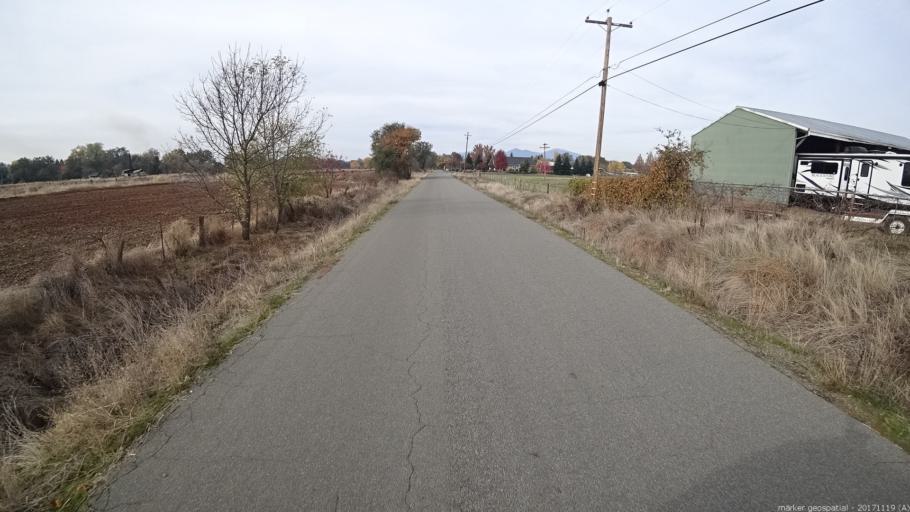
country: US
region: California
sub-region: Shasta County
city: Anderson
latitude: 40.5223
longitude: -122.3356
